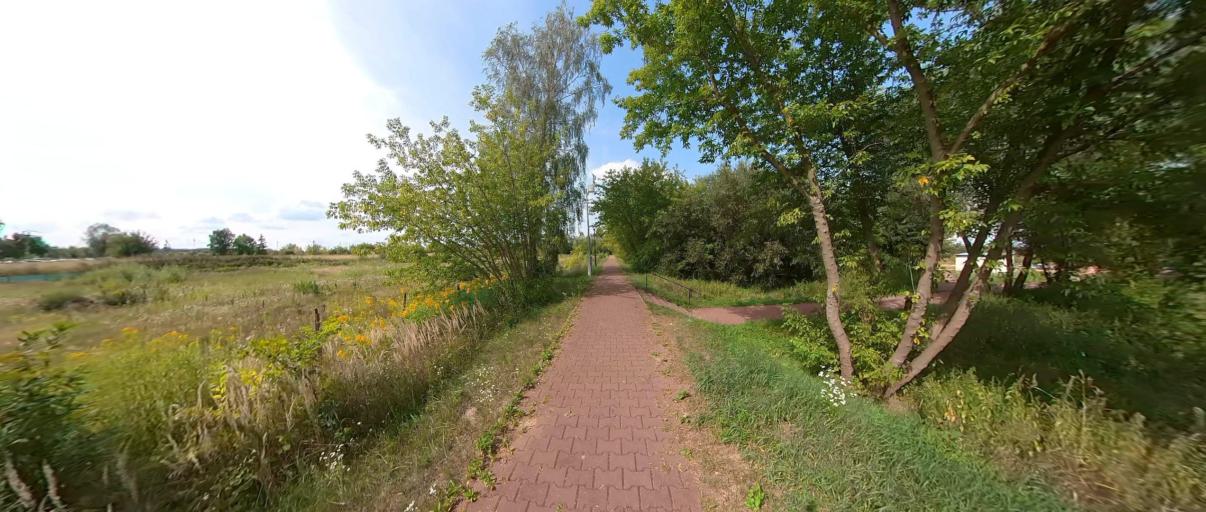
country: PL
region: Masovian Voivodeship
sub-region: Powiat bialobrzeski
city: Bialobrzegi
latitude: 51.6540
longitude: 20.9544
